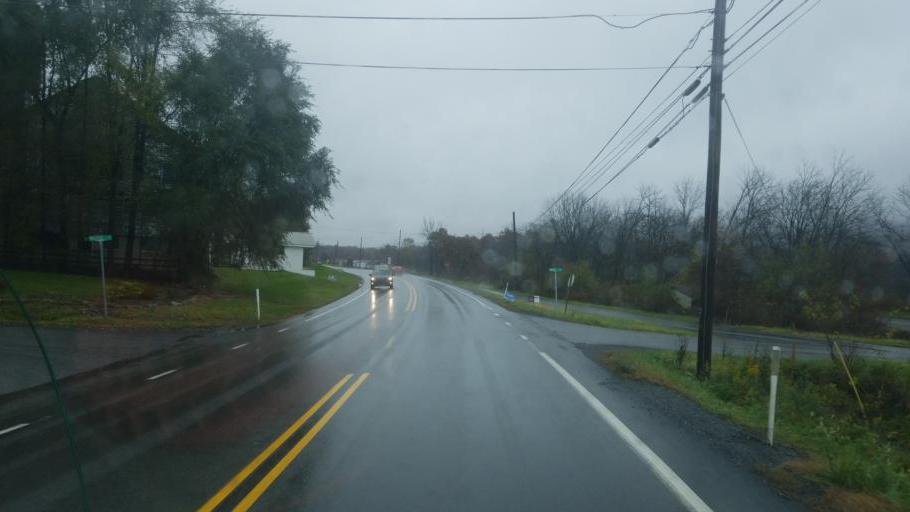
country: US
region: Pennsylvania
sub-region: Clinton County
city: Mill Hall
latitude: 41.0758
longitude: -77.5668
